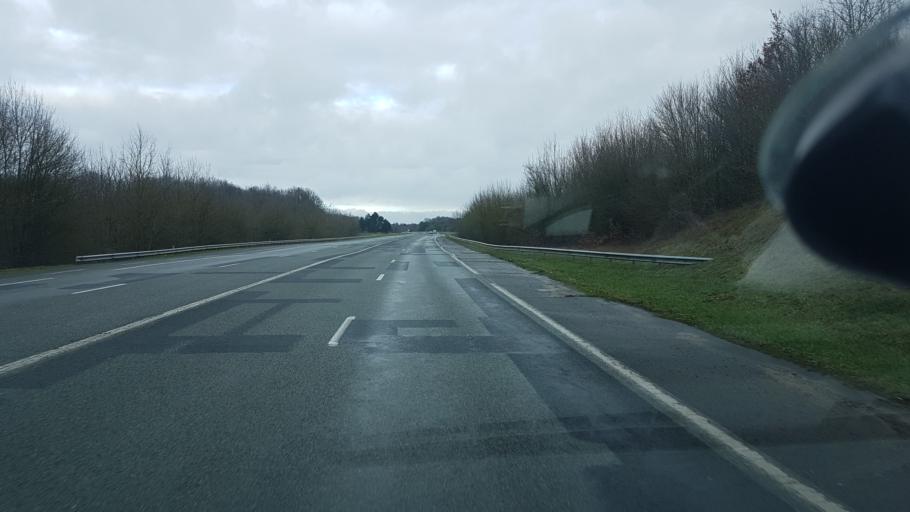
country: FR
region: Centre
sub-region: Departement du Loiret
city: Dordives
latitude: 48.1619
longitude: 2.7646
